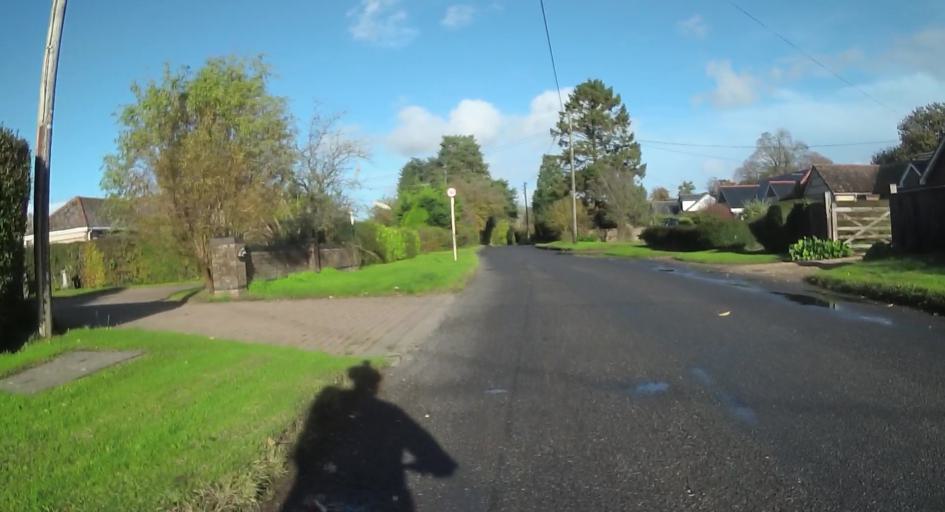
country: GB
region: England
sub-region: Hampshire
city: Four Marks
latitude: 51.1308
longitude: -1.0569
